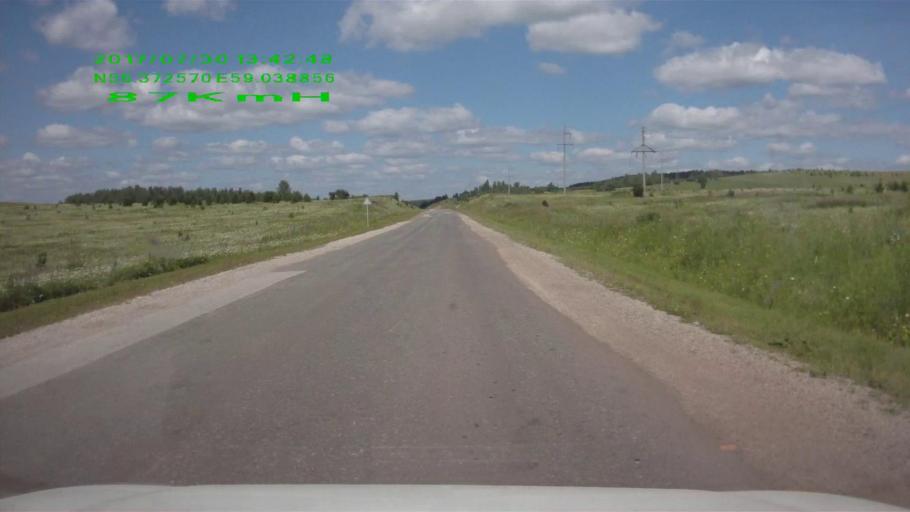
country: RU
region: Sverdlovsk
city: Mikhaylovsk
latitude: 56.3729
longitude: 59.0389
